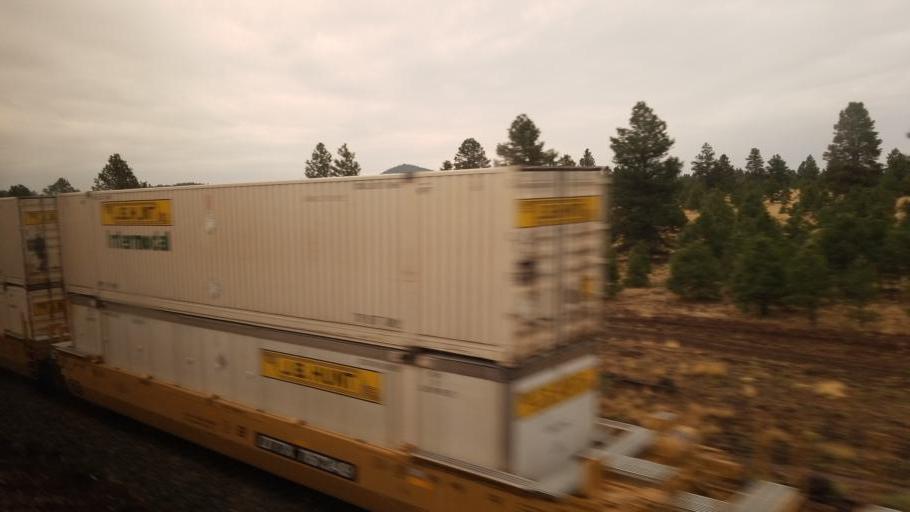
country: US
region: Arizona
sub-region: Coconino County
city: Parks
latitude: 35.2504
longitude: -111.9551
